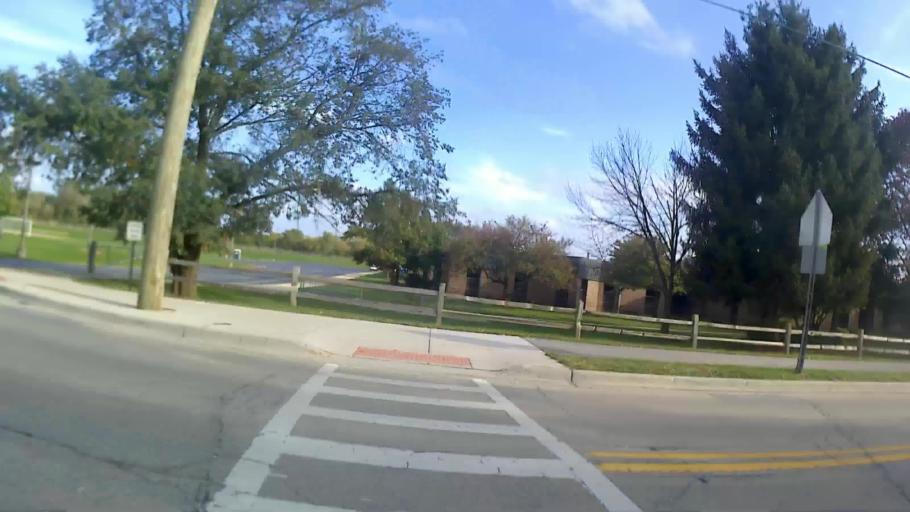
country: US
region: Illinois
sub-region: DuPage County
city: Warrenville
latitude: 41.8093
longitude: -88.1775
